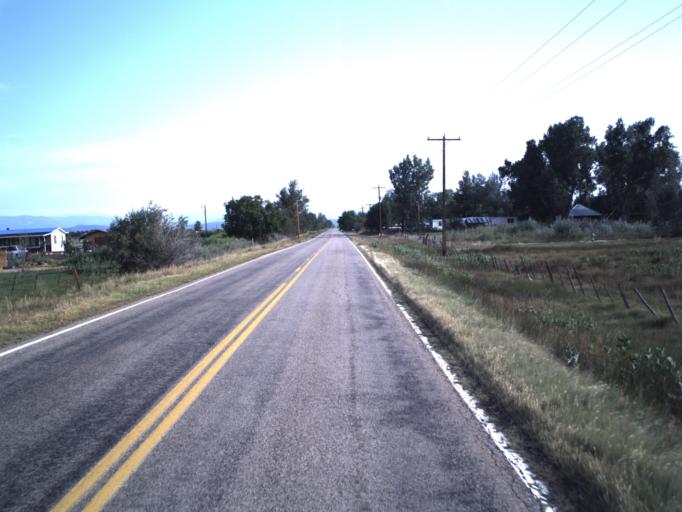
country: US
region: Utah
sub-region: Duchesne County
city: Duchesne
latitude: 40.3461
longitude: -110.2752
